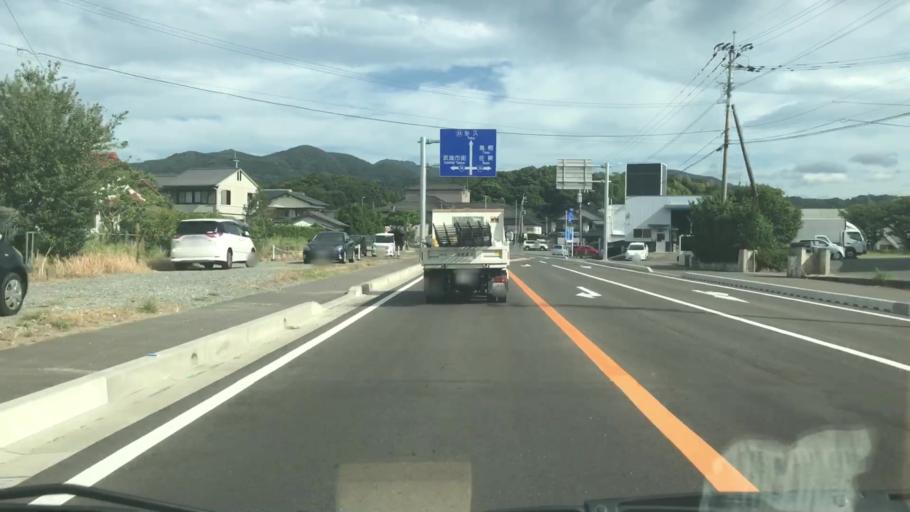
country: JP
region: Saga Prefecture
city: Takeocho-takeo
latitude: 33.2186
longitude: 130.0613
